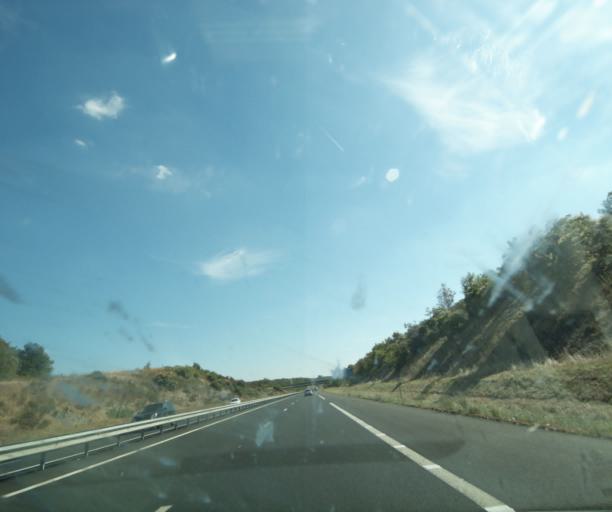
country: FR
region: Limousin
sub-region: Departement de la Correze
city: Brive-la-Gaillarde
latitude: 45.0481
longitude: 1.5154
